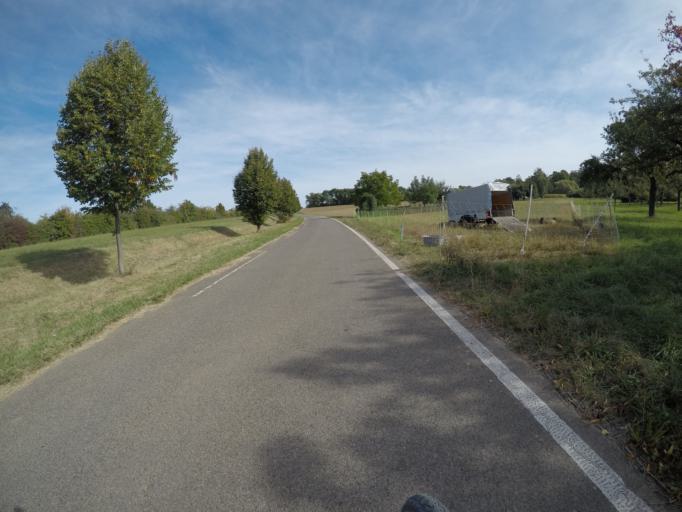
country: DE
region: Baden-Wuerttemberg
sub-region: Regierungsbezirk Stuttgart
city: Schwieberdingen
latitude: 48.8620
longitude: 9.0953
